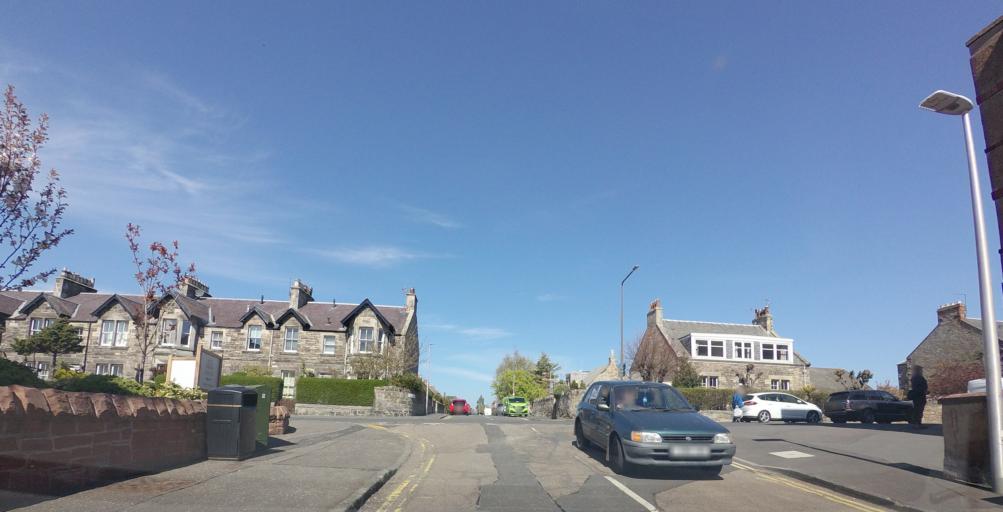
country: GB
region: Scotland
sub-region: East Lothian
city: Gullane
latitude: 56.0353
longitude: -2.8296
